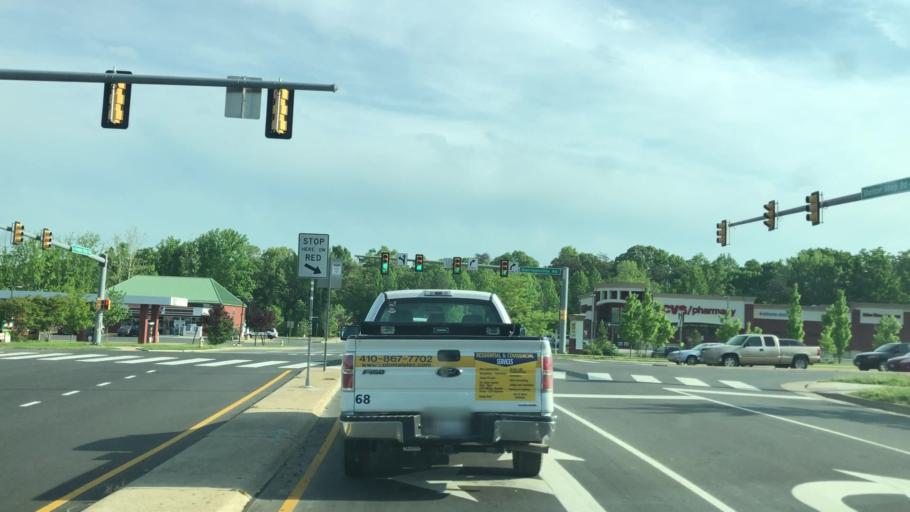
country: US
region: Virginia
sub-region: Stafford County
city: Stafford
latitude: 38.4685
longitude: -77.4608
